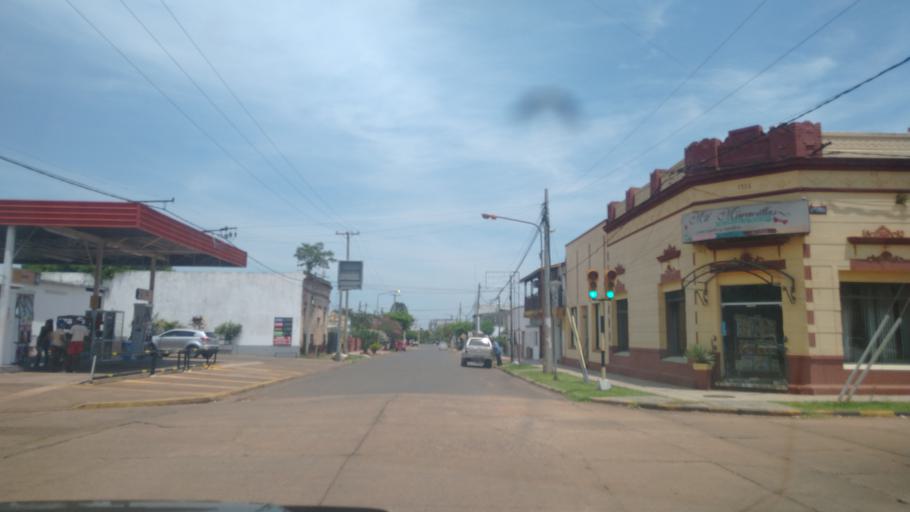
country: AR
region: Corrientes
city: Santo Tome
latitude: -28.5488
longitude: -56.0434
